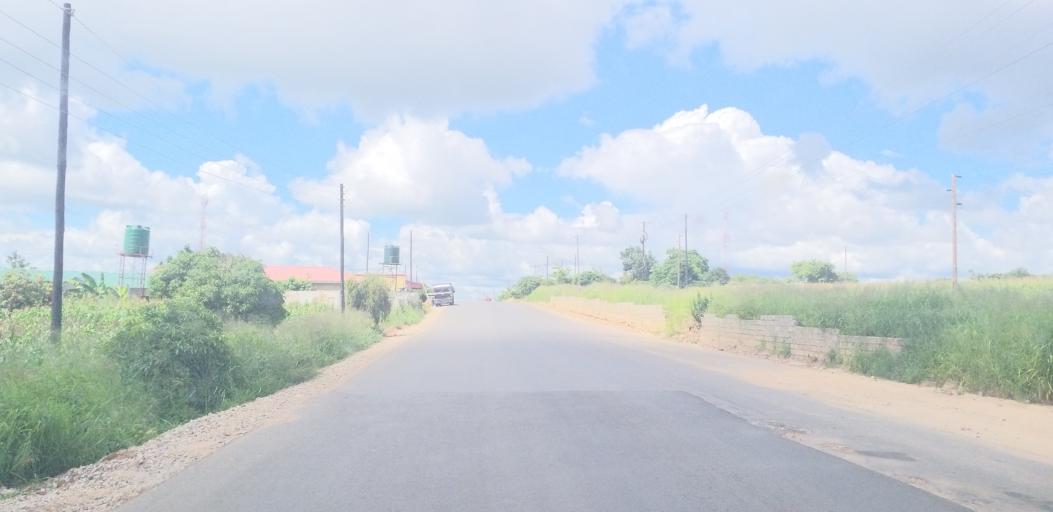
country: ZM
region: Lusaka
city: Lusaka
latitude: -15.3528
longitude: 28.3247
